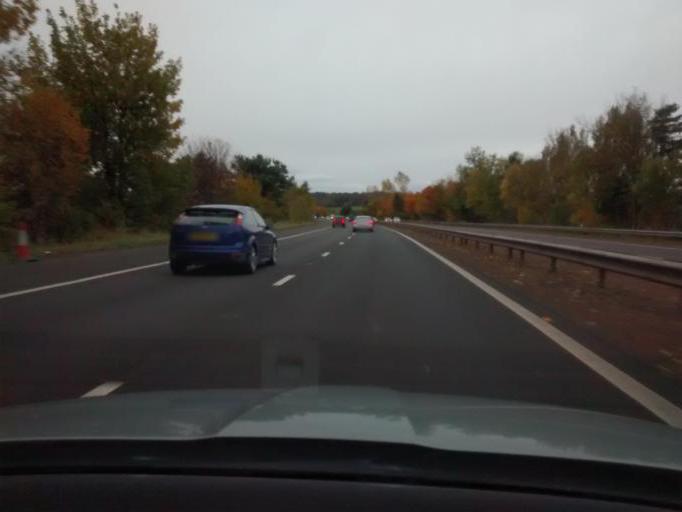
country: GB
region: Scotland
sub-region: Falkirk
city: Grangemouth
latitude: 56.0070
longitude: -3.7396
